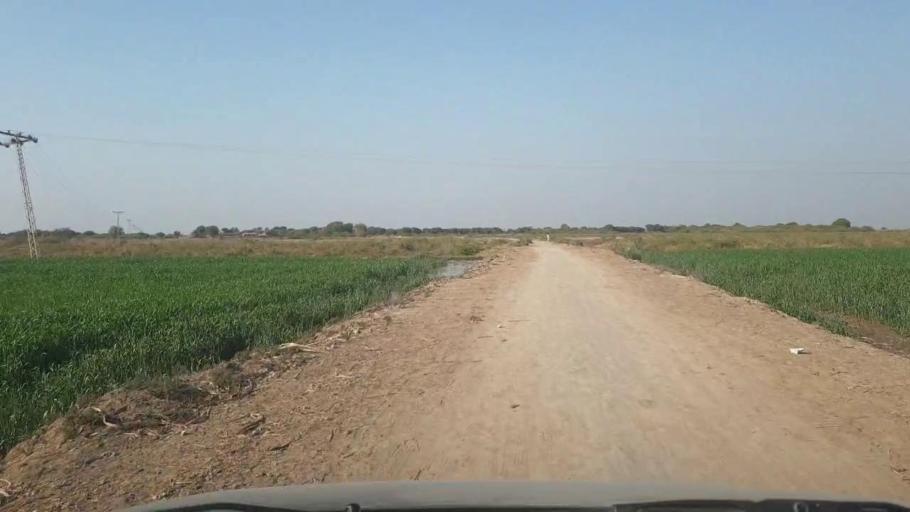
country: PK
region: Sindh
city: Chambar
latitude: 25.2980
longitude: 68.8630
